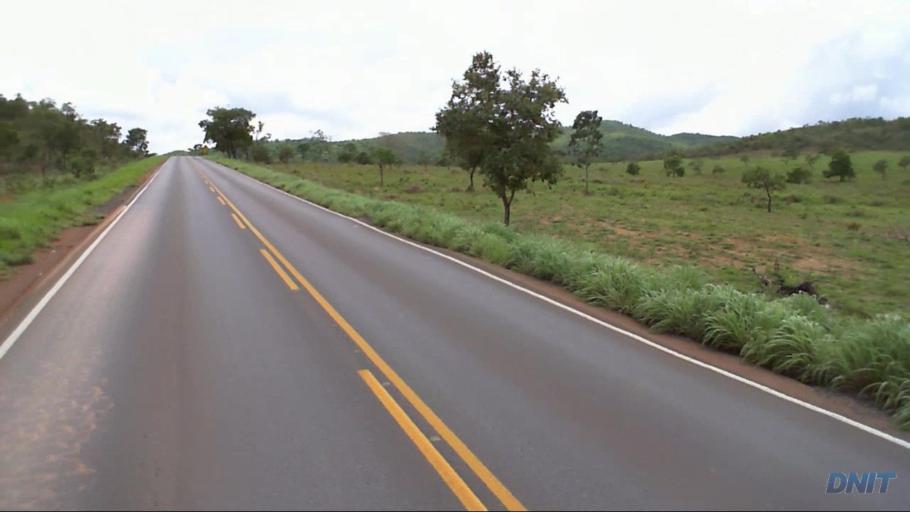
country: BR
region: Goias
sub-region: Padre Bernardo
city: Padre Bernardo
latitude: -15.4414
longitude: -48.1972
